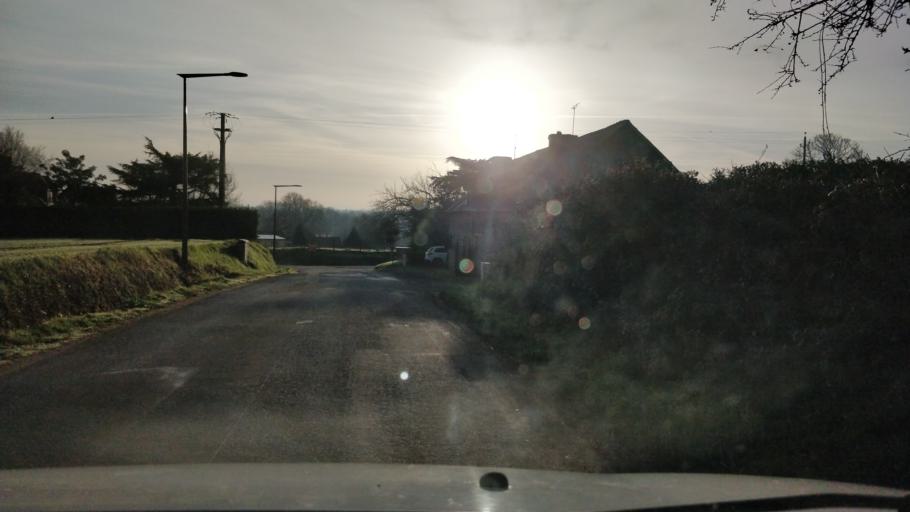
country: FR
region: Brittany
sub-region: Departement d'Ille-et-Vilaine
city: Bais
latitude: 48.0090
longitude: -1.2971
